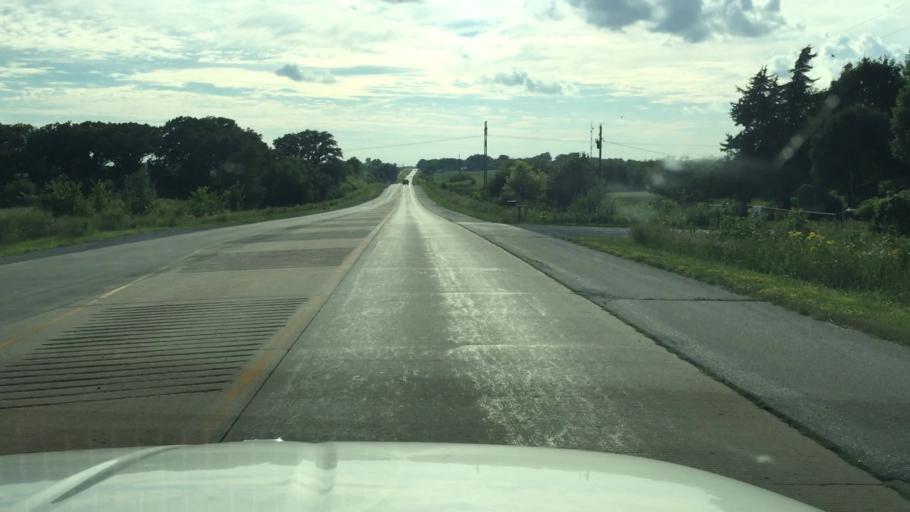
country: US
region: Iowa
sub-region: Johnson County
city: Iowa City
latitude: 41.6711
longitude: -91.4551
